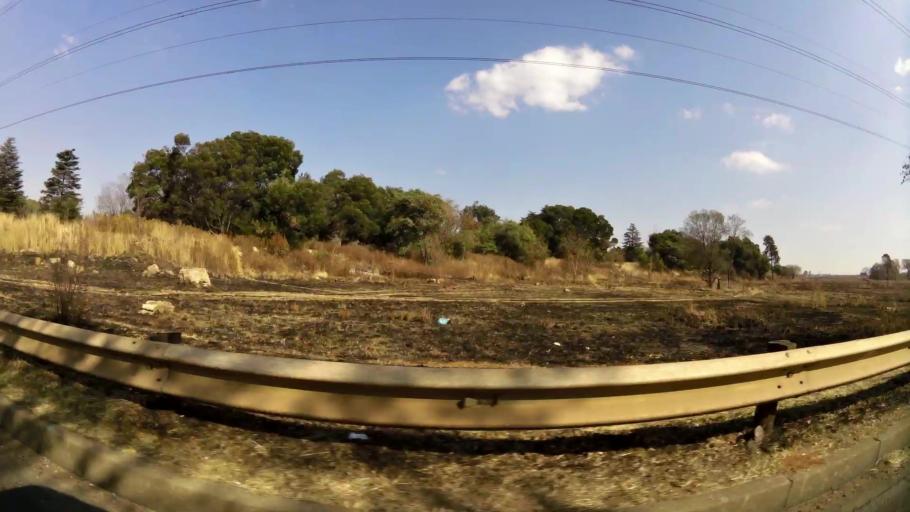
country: ZA
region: Gauteng
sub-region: City of Johannesburg Metropolitan Municipality
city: Modderfontein
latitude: -26.0996
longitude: 28.2138
